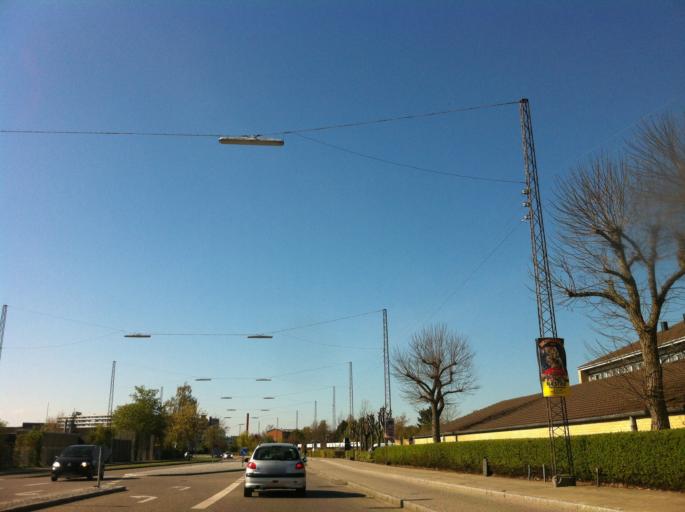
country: DK
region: Zealand
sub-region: Naestved Kommune
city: Naestved
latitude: 55.2141
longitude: 11.7602
